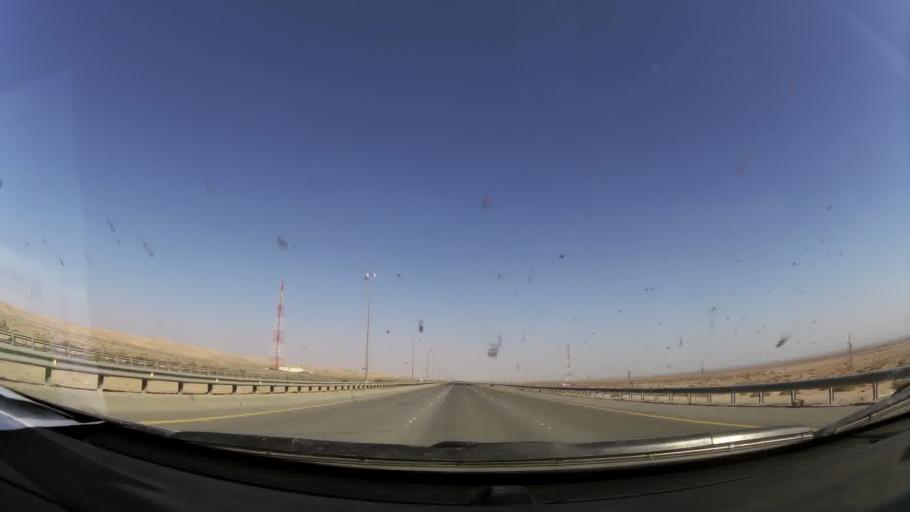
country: KW
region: Al Asimah
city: Kuwait City
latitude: 29.5317
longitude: 47.8296
